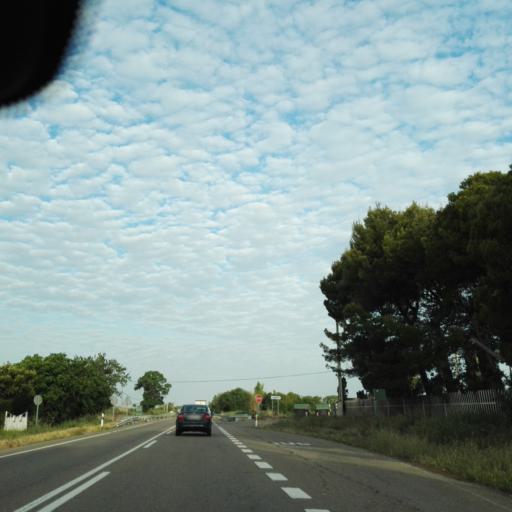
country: ES
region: Aragon
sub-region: Provincia de Zaragoza
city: Oliver-Valdefierro, Oliver, Valdefierro
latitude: 41.6638
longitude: -0.9690
